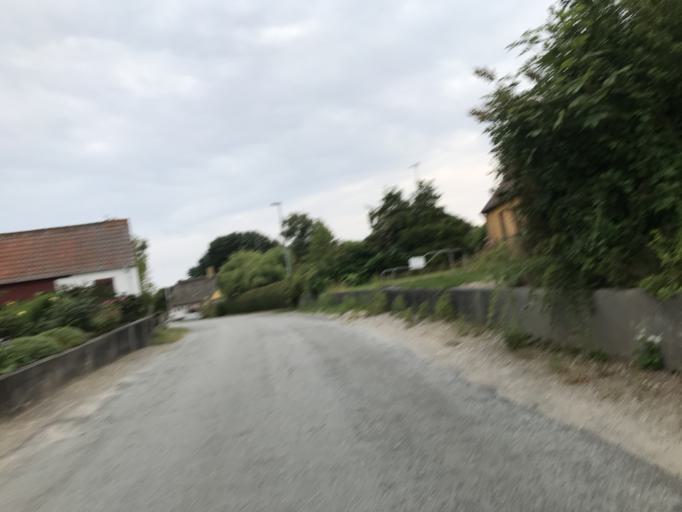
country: DK
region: South Denmark
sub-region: Faaborg-Midtfyn Kommune
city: Faaborg
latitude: 54.9387
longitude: 10.2537
